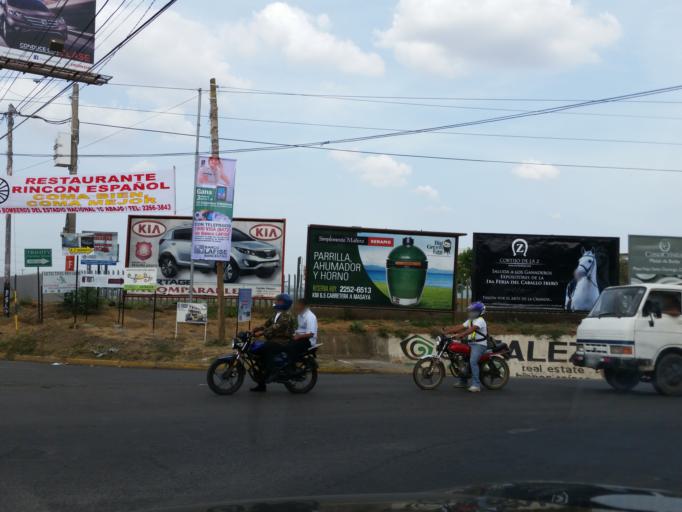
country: NI
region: Managua
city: Managua
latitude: 12.1050
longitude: -86.2509
